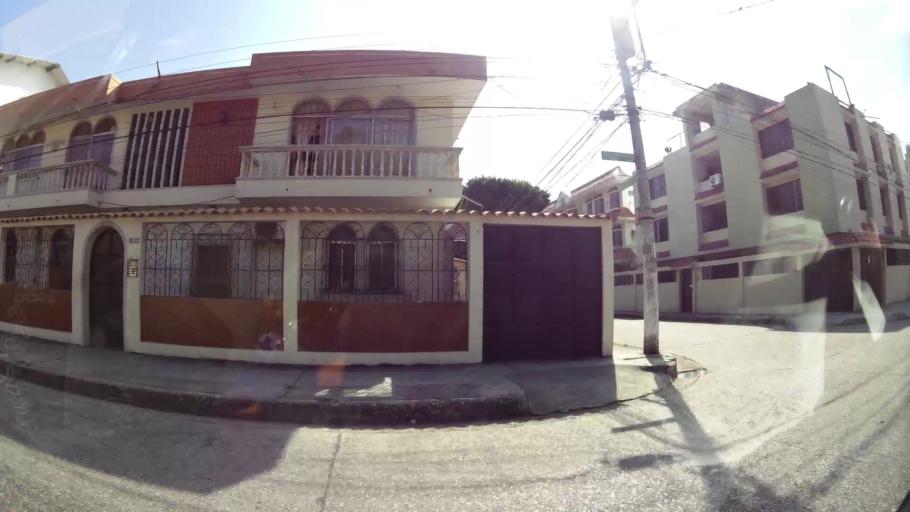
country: EC
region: Guayas
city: Guayaquil
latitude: -2.2284
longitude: -79.8918
